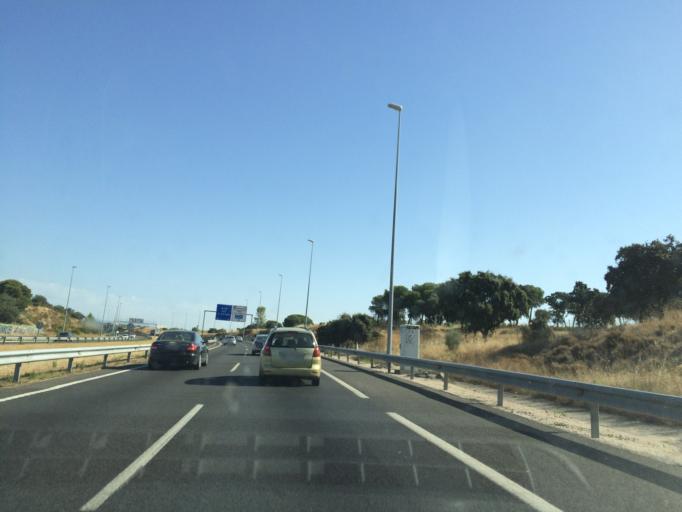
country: ES
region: Madrid
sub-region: Provincia de Madrid
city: Boadilla del Monte
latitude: 40.4371
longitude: -3.8781
